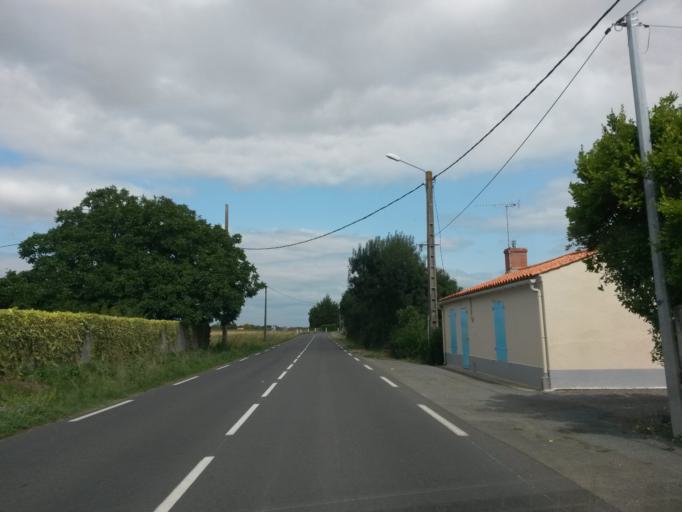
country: FR
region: Pays de la Loire
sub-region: Departement de la Vendee
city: Longeville-sur-Mer
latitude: 46.4226
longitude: -1.5171
